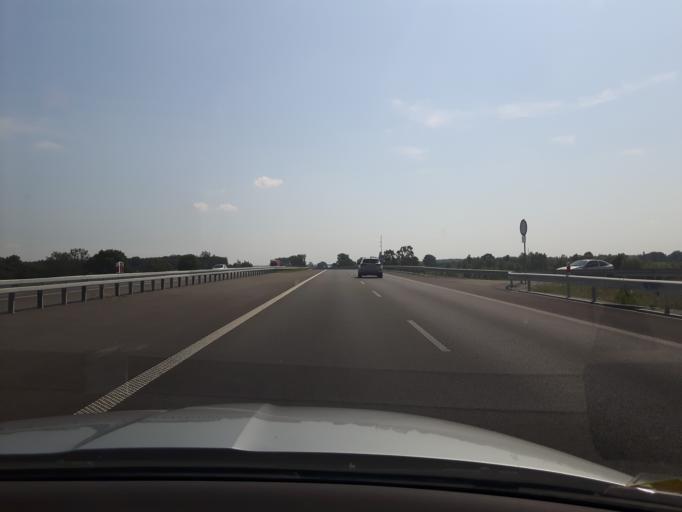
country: PL
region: Warmian-Masurian Voivodeship
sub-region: Powiat elblaski
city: Gronowo Elblaskie
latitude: 54.1667
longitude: 19.2366
